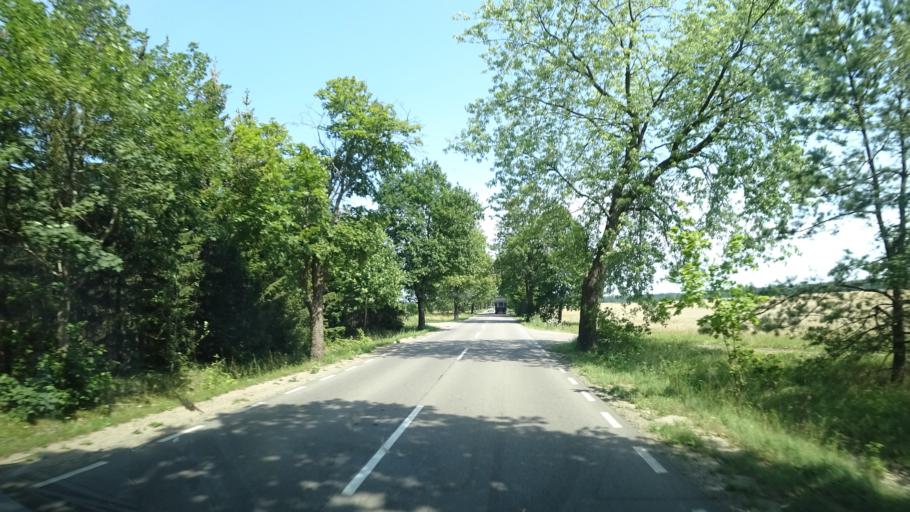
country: PL
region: Pomeranian Voivodeship
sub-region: Powiat koscierski
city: Lipusz
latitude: 54.1240
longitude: 17.8521
